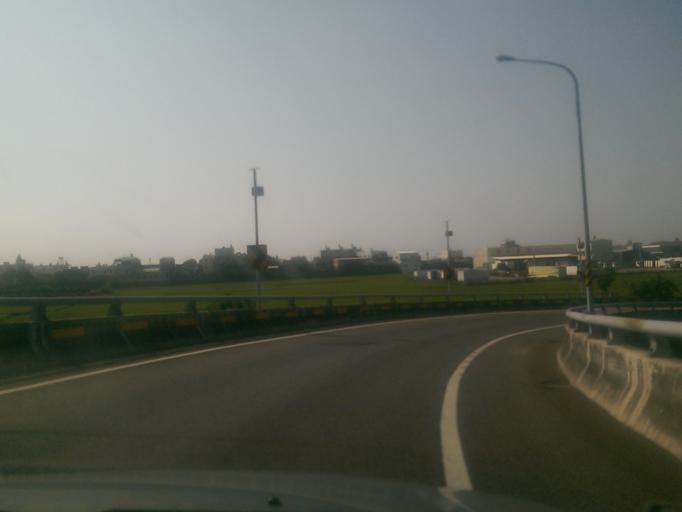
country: TW
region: Taiwan
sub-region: Changhua
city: Chang-hua
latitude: 24.0854
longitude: 120.5961
